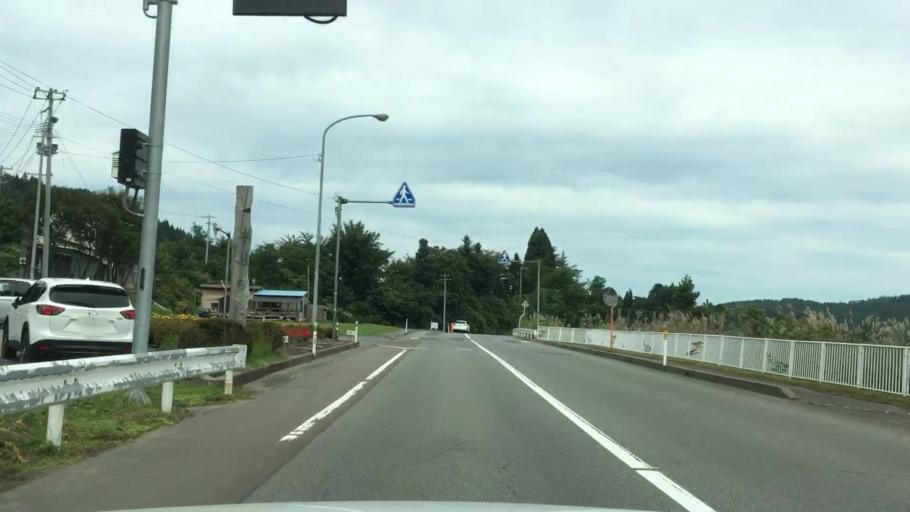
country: JP
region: Aomori
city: Shimokizukuri
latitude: 40.7502
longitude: 140.2294
